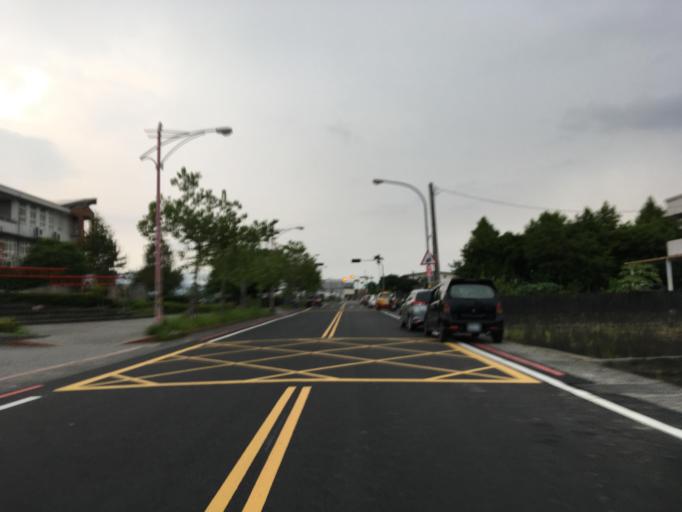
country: TW
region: Taiwan
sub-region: Yilan
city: Yilan
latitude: 24.6647
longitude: 121.7645
